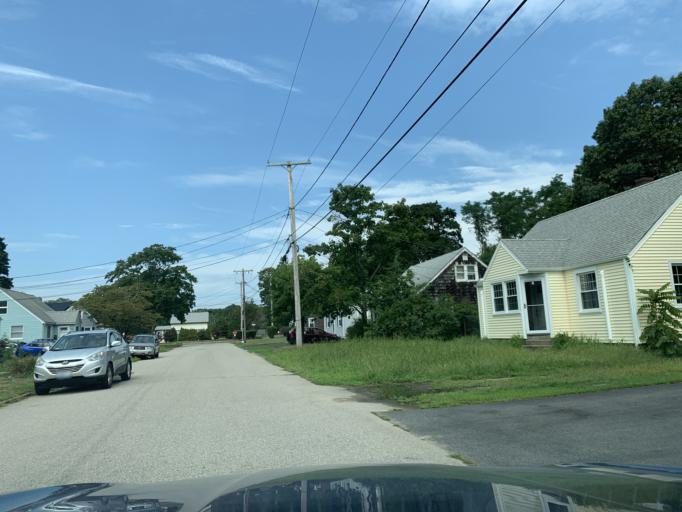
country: US
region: Rhode Island
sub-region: Kent County
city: East Greenwich
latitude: 41.6157
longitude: -71.4689
